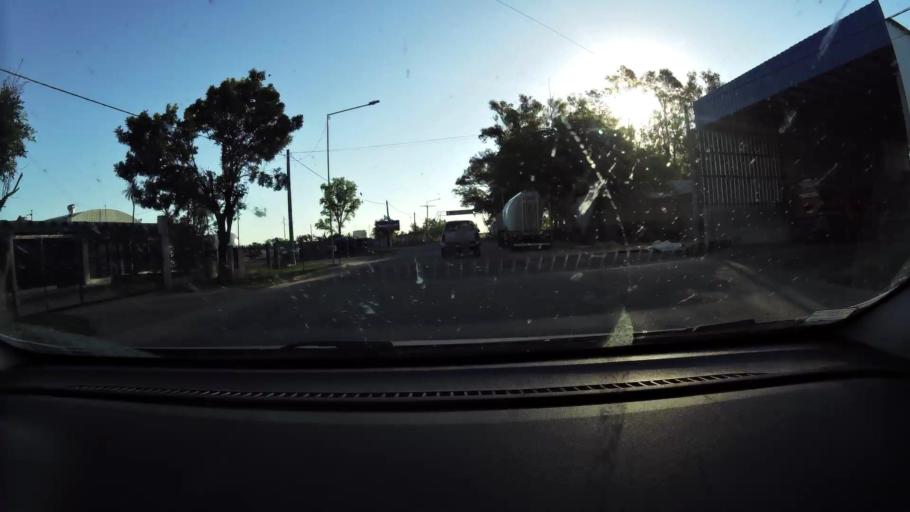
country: AR
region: Cordoba
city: Saturnino M. Laspiur
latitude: -31.7077
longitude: -62.4889
